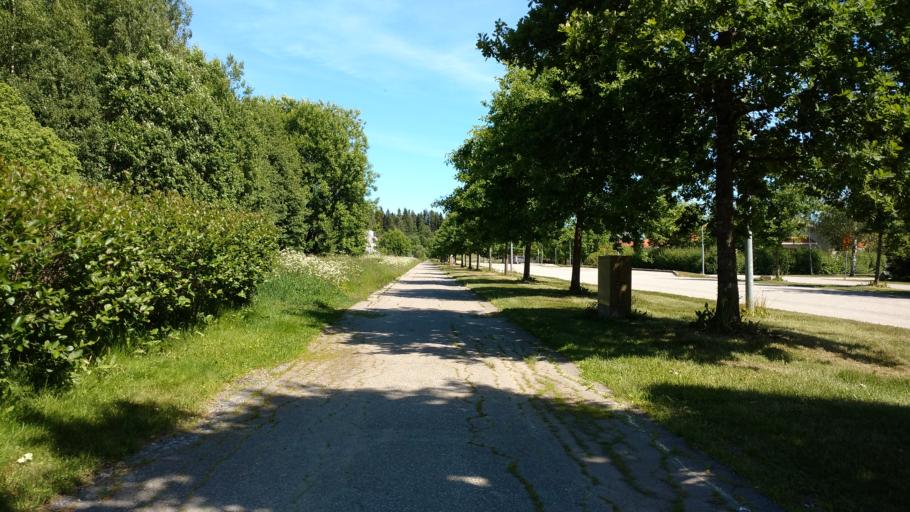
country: FI
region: Varsinais-Suomi
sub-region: Salo
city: Salo
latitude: 60.4025
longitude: 23.1423
